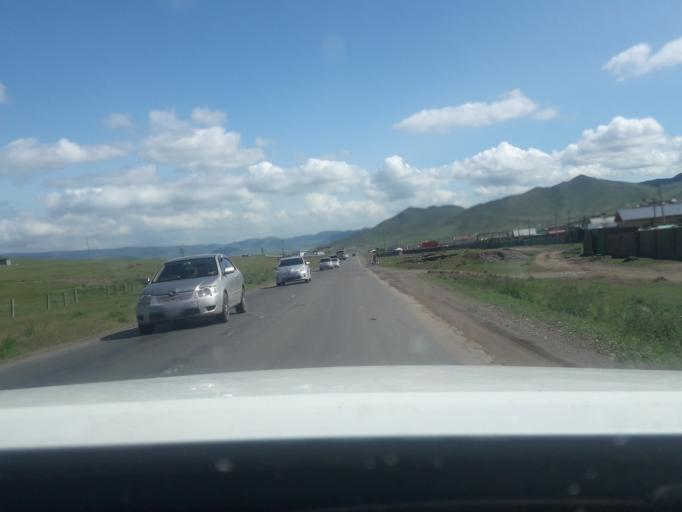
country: MN
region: Ulaanbaatar
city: Ulaanbaatar
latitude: 47.9070
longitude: 106.6384
